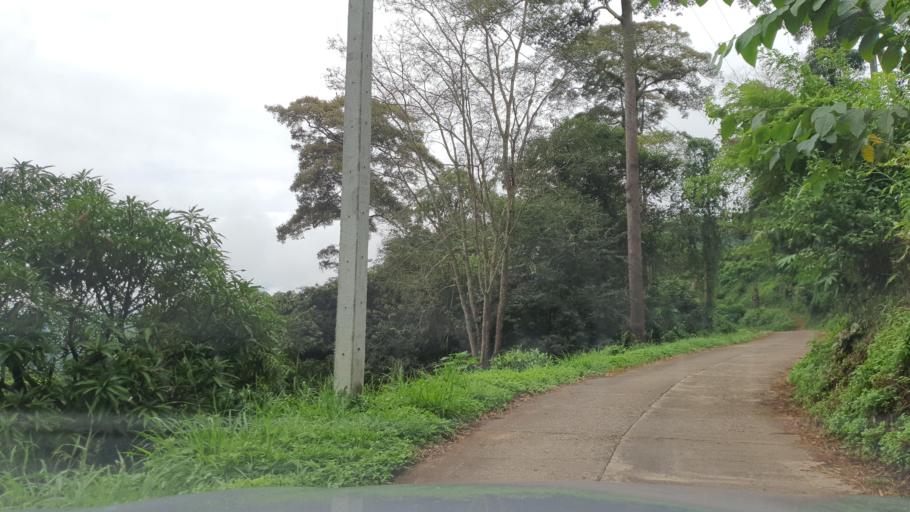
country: TH
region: Chiang Mai
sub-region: Amphoe Chiang Dao
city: Chiang Dao
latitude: 19.2626
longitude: 98.9206
